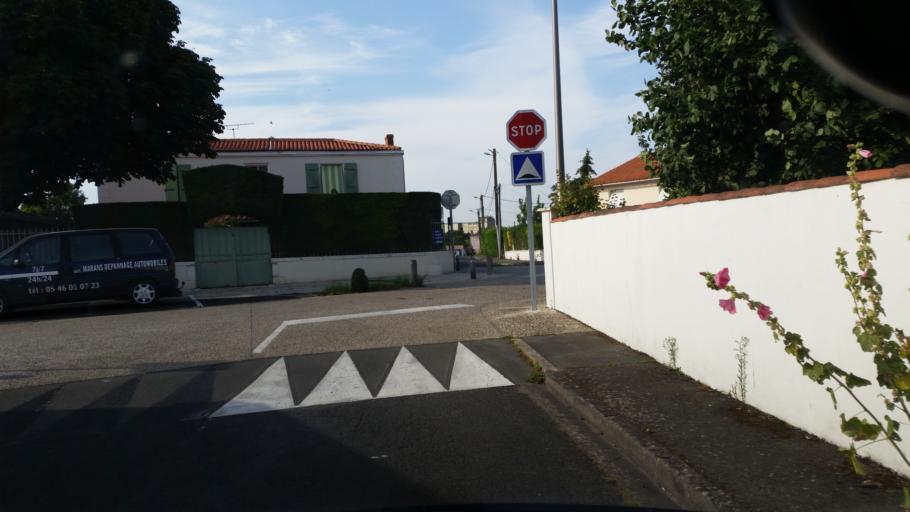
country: FR
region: Poitou-Charentes
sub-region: Departement de la Charente-Maritime
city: Marans
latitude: 46.3076
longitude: -1.0016
